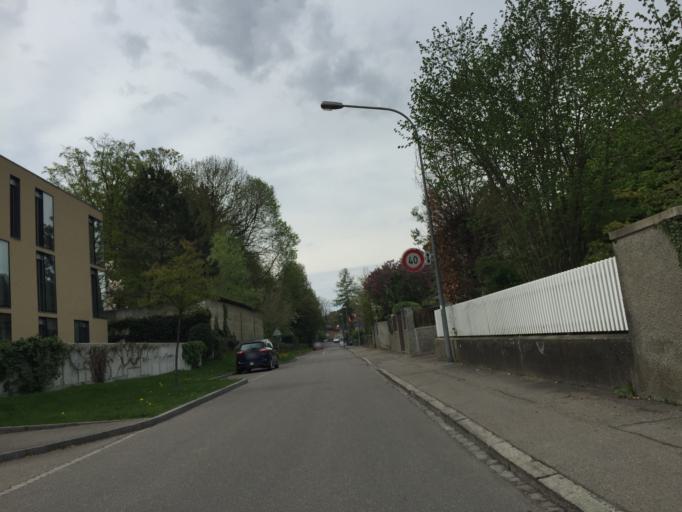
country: CH
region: Bern
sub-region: Bern-Mittelland District
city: Muri
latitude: 46.9337
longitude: 7.4785
